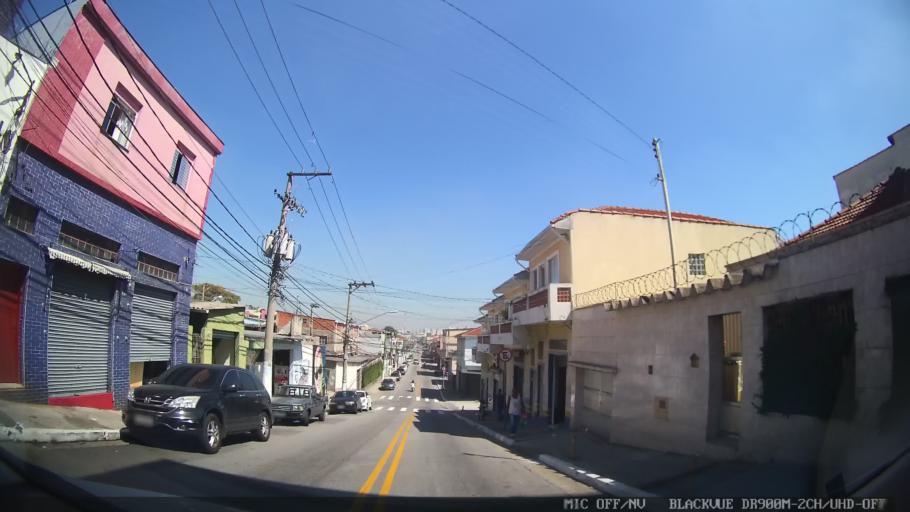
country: BR
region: Sao Paulo
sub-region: Sao Paulo
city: Sao Paulo
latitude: -23.4940
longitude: -46.6567
